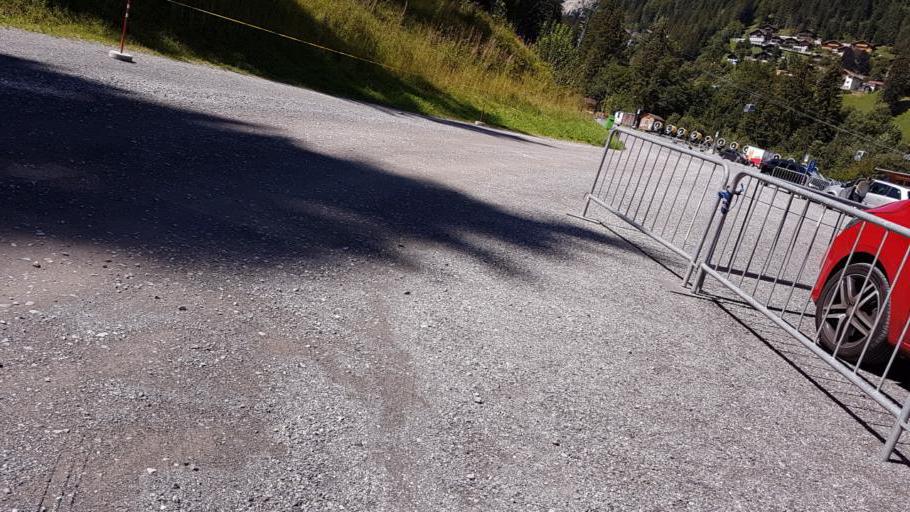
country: CH
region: Bern
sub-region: Frutigen-Niedersimmental District
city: Adelboden
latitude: 46.4871
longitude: 7.5615
